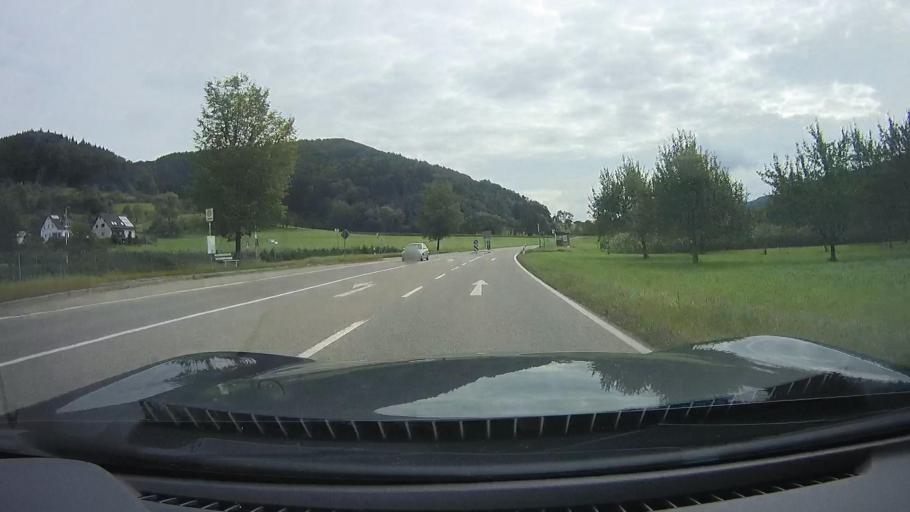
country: DE
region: Baden-Wuerttemberg
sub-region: Regierungsbezirk Stuttgart
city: Sulzbach an der Murr
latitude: 49.0166
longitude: 9.4700
